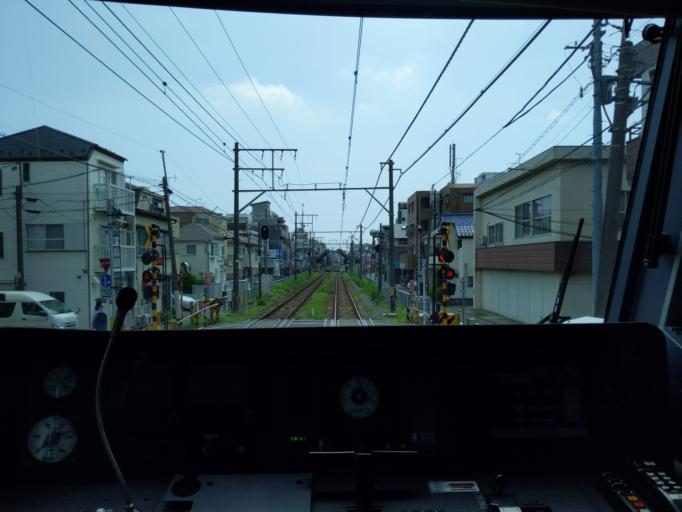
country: JP
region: Kanagawa
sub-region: Kawasaki-shi
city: Kawasaki
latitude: 35.5769
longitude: 139.6789
